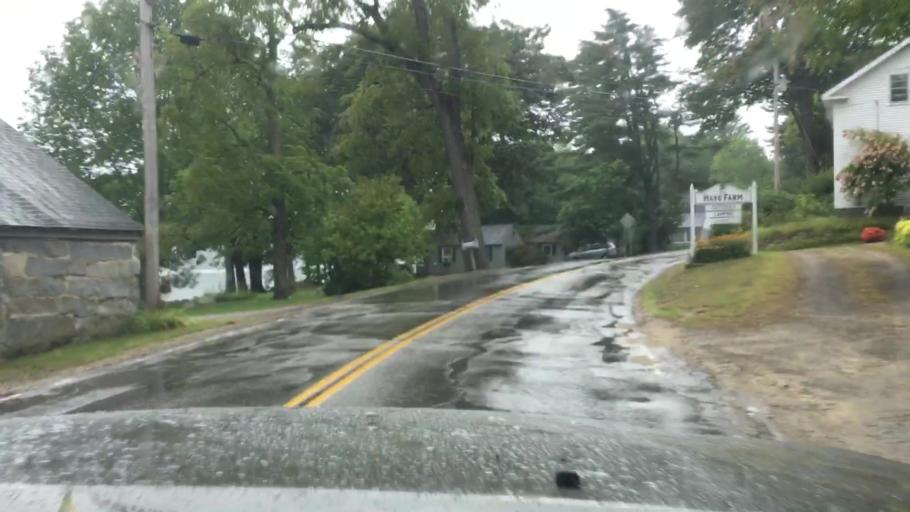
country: US
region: New Hampshire
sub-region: Belknap County
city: Meredith
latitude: 43.6690
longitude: -71.5346
